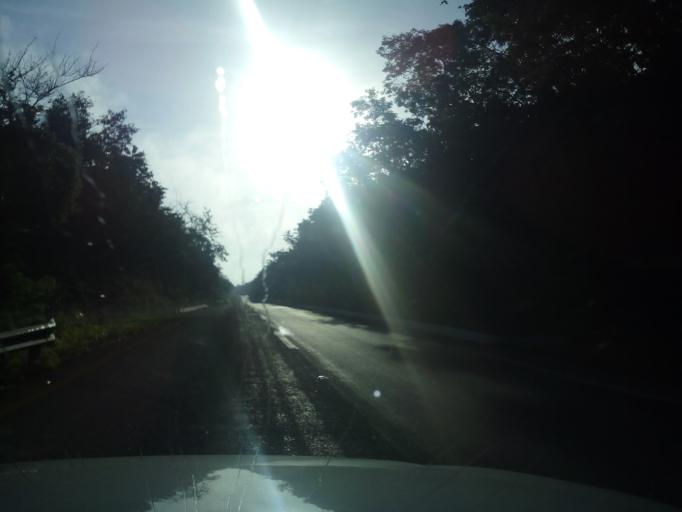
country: MX
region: Yucatan
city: Tunkas
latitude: 20.7627
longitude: -88.7880
